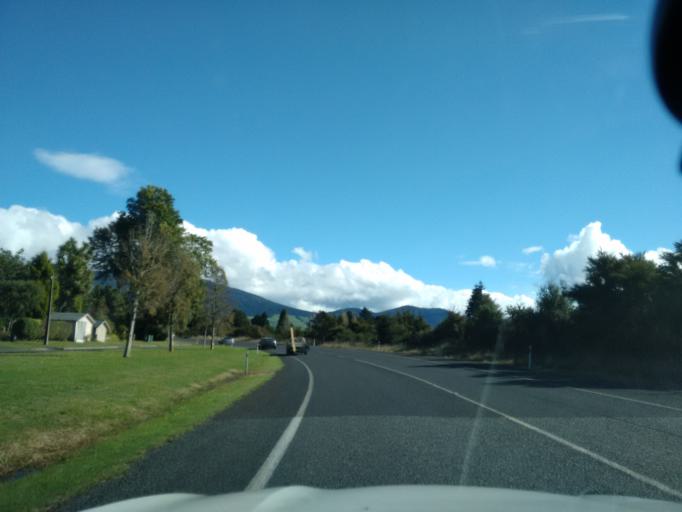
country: NZ
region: Waikato
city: Turangi
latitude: -38.9826
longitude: 175.8210
